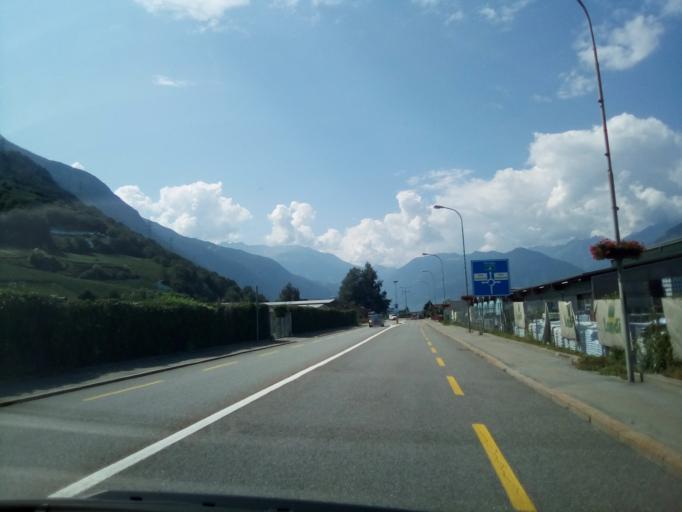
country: CH
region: Valais
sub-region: Martigny District
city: Saxon
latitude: 46.1471
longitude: 7.1695
